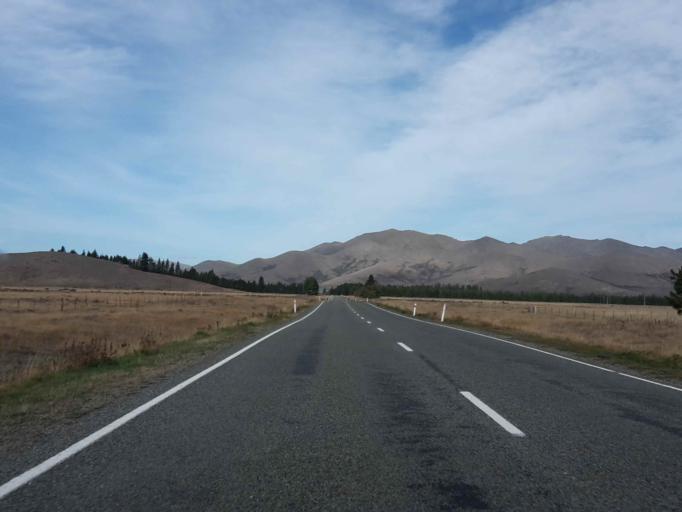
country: NZ
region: Canterbury
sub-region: Timaru District
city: Pleasant Point
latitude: -44.0773
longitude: 170.5263
